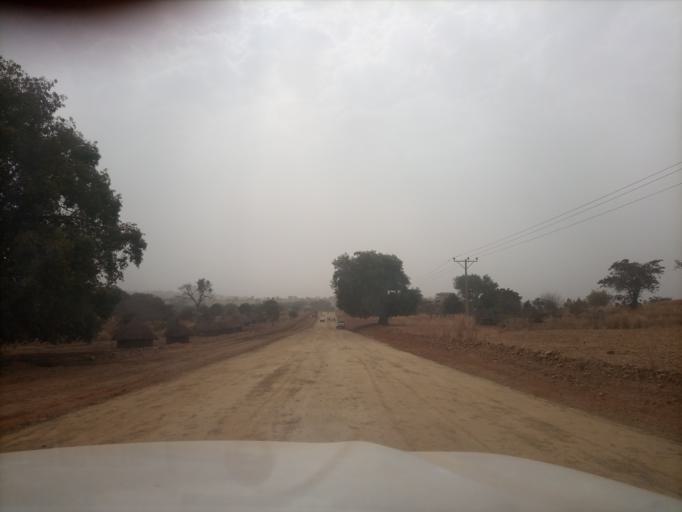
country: ET
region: Oromiya
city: Mendi
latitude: 10.1352
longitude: 35.1236
